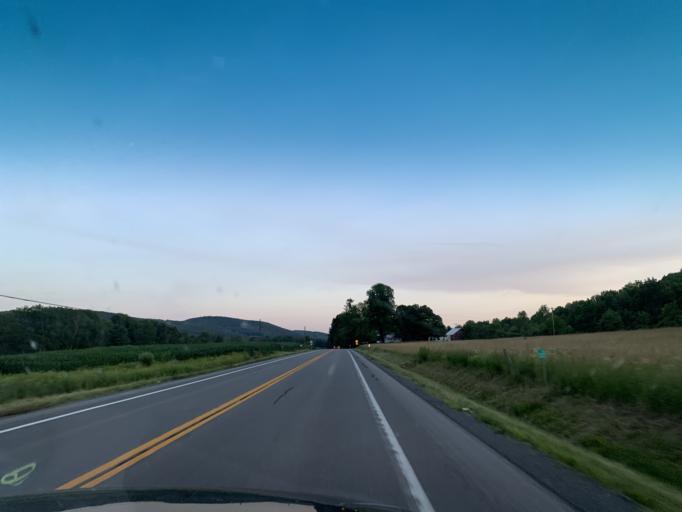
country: US
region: New York
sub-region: Oneida County
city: Waterville
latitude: 42.7976
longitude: -75.2551
